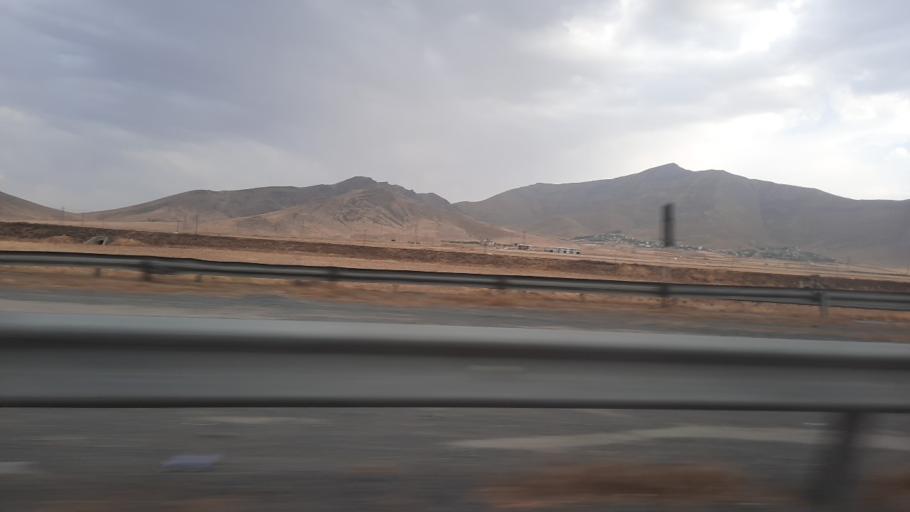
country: IR
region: Markazi
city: Arak
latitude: 34.0233
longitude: 49.5825
